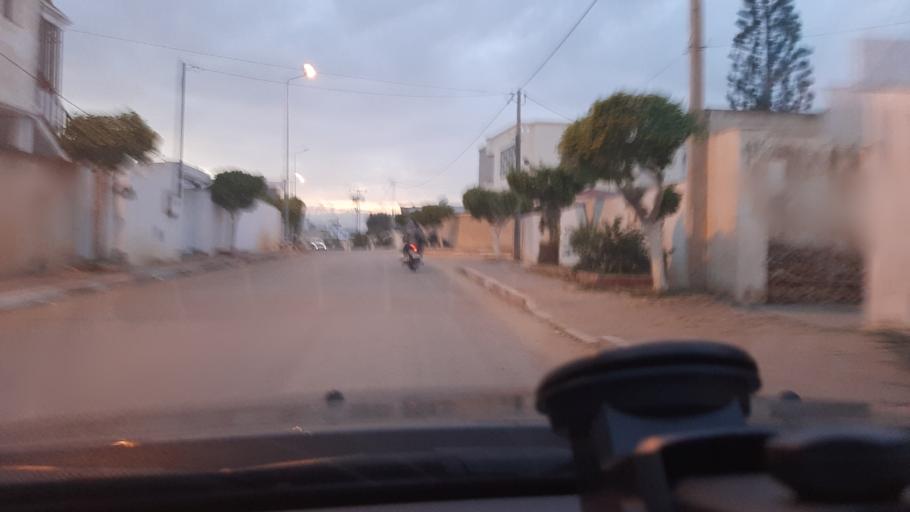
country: TN
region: Safaqis
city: Sfax
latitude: 34.7646
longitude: 10.6970
